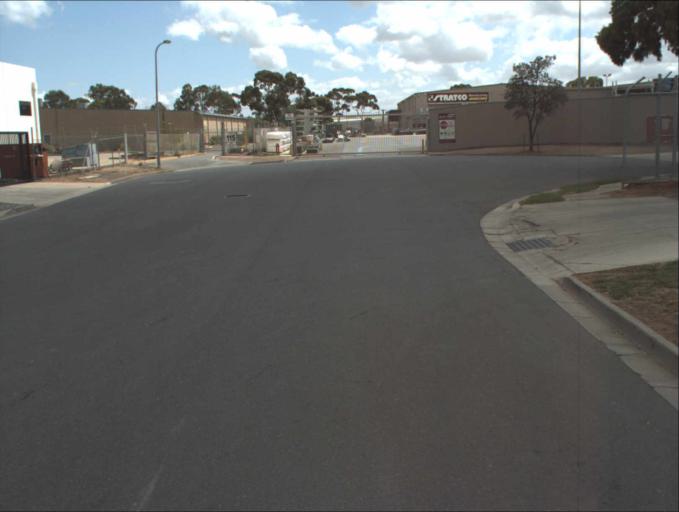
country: AU
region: South Australia
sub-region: Port Adelaide Enfield
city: Enfield
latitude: -34.8402
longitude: 138.5964
